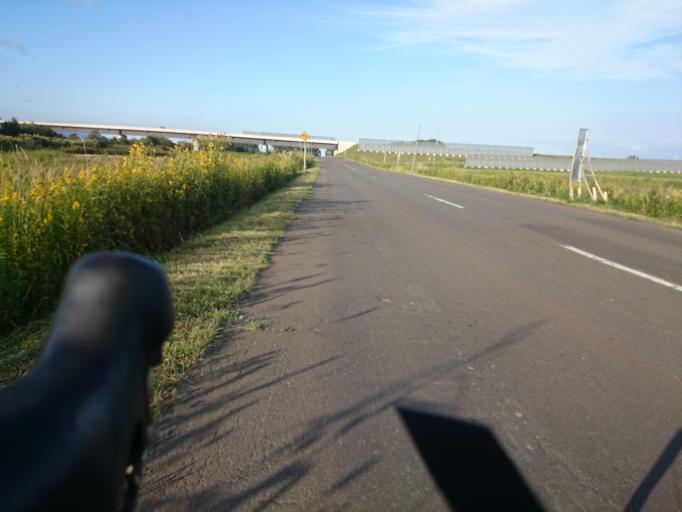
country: JP
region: Hokkaido
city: Tobetsu
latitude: 43.1817
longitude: 141.5560
